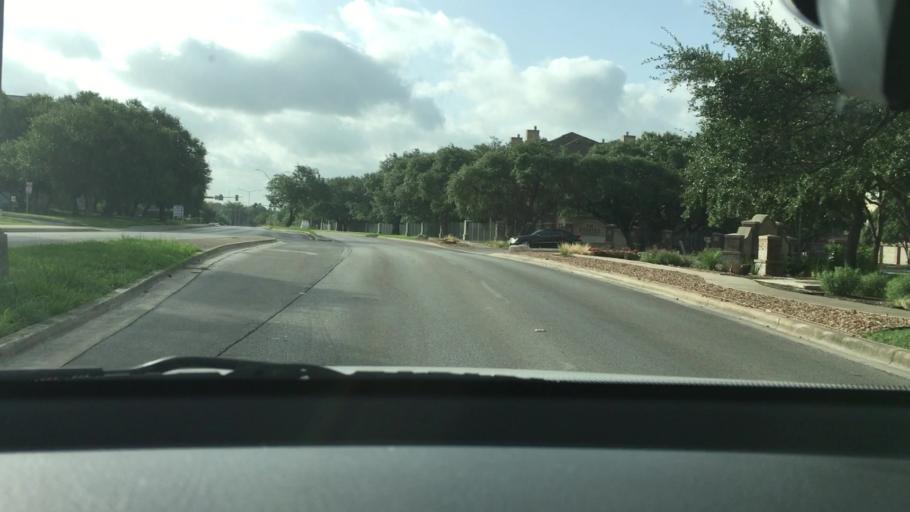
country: US
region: Texas
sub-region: Bexar County
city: Hollywood Park
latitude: 29.6031
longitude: -98.4614
